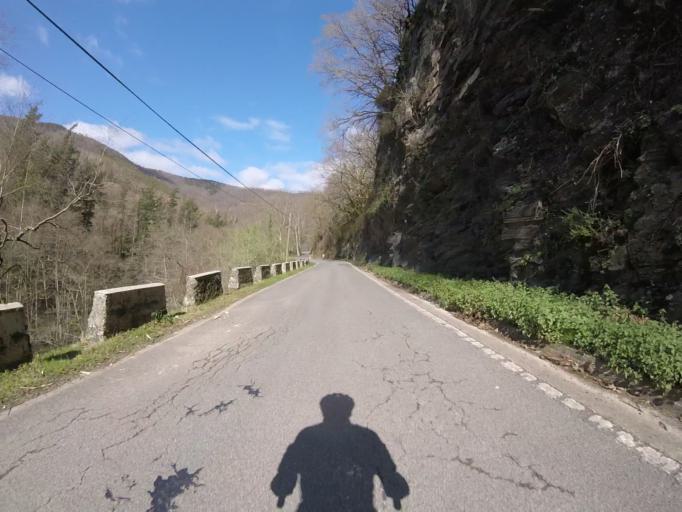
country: ES
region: Navarre
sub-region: Provincia de Navarra
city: Goizueta
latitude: 43.1430
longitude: -1.8487
